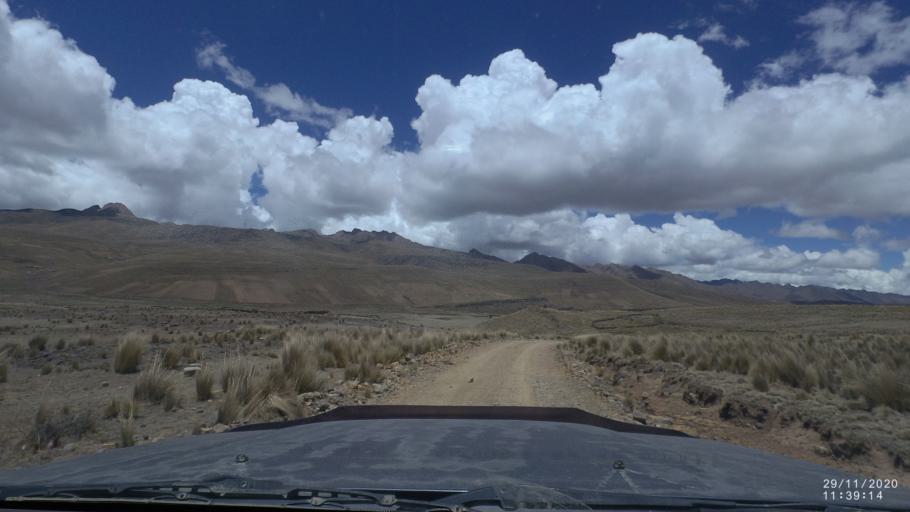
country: BO
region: Cochabamba
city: Cochabamba
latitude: -17.1978
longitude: -66.2387
